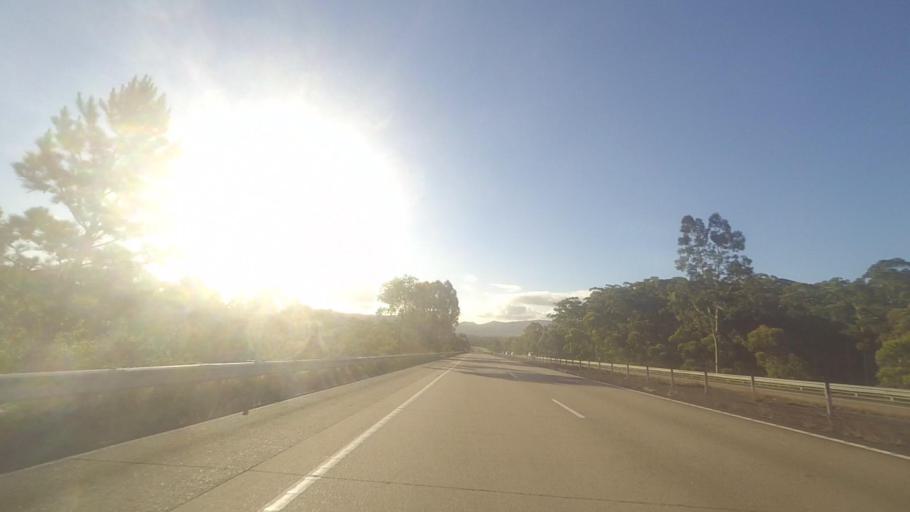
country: AU
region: New South Wales
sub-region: Great Lakes
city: Bulahdelah
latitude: -32.3875
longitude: 152.2436
